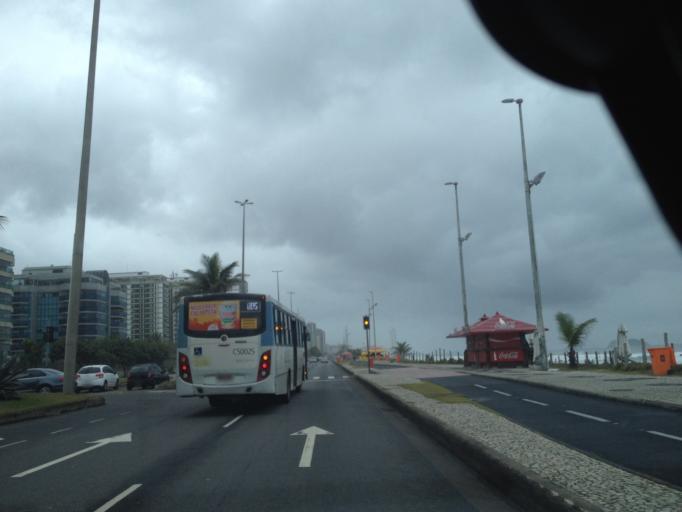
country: BR
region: Rio de Janeiro
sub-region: Rio De Janeiro
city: Rio de Janeiro
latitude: -23.0104
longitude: -43.3489
